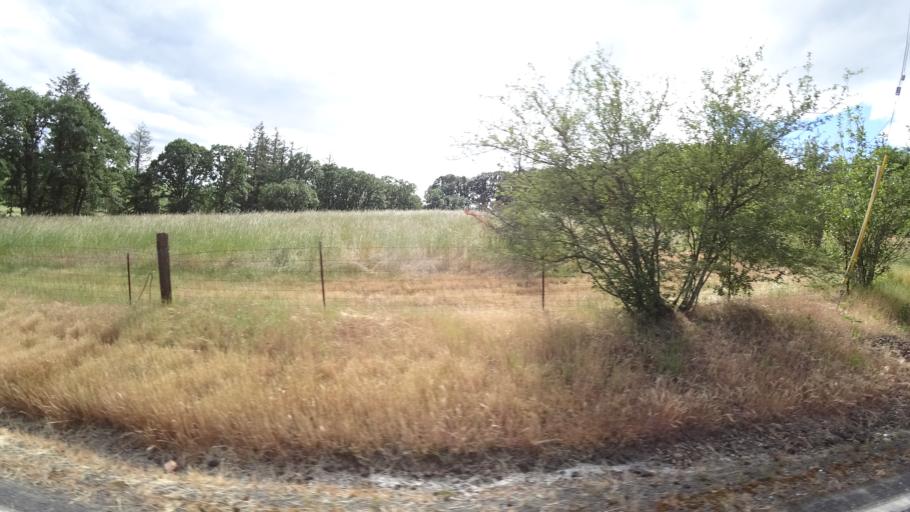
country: US
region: Oregon
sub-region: Washington County
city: Bethany
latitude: 45.5803
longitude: -122.8404
